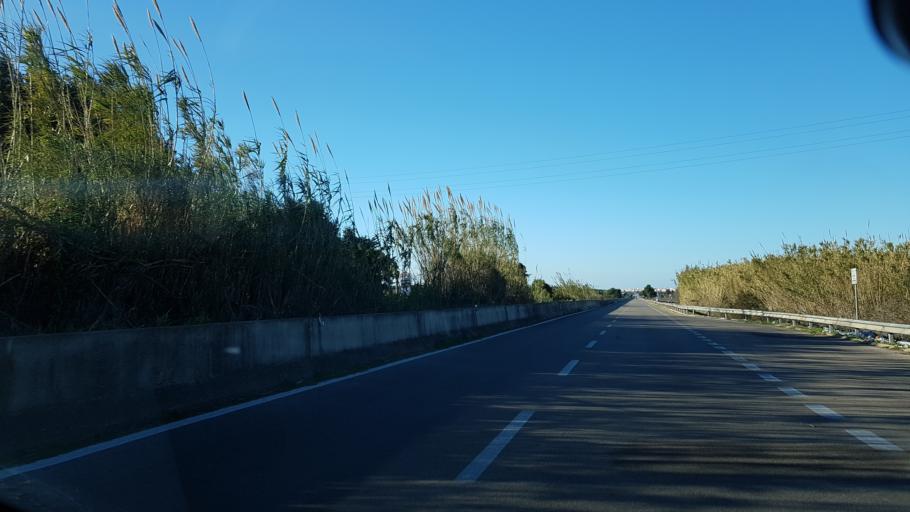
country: IT
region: Apulia
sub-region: Provincia di Lecce
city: Alezio
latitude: 40.0169
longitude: 18.0462
